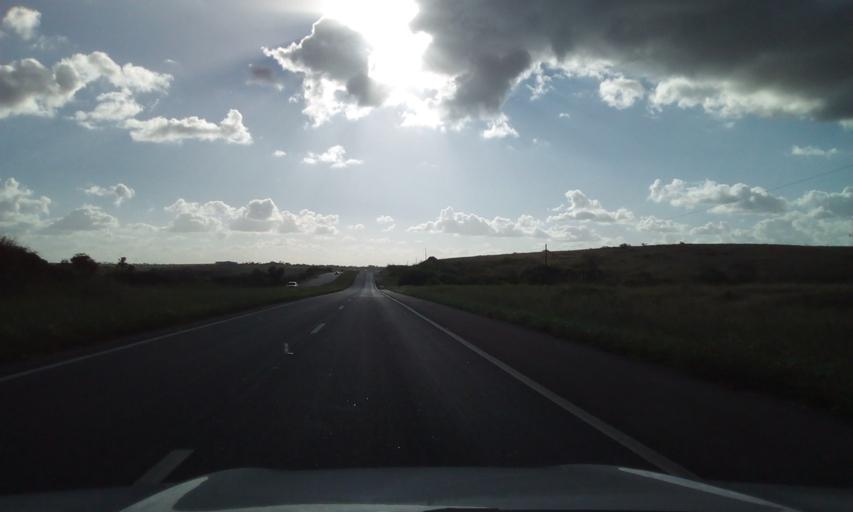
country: BR
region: Paraiba
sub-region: Cruz Do Espirito Santo
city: Cruz do Espirito Santo
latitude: -7.1945
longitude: -35.1750
